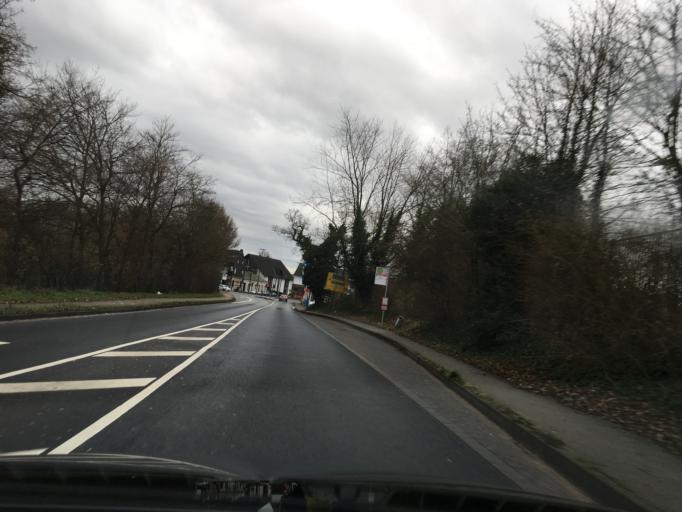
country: DE
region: North Rhine-Westphalia
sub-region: Regierungsbezirk Dusseldorf
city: Erkrath
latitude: 51.2028
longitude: 6.9055
